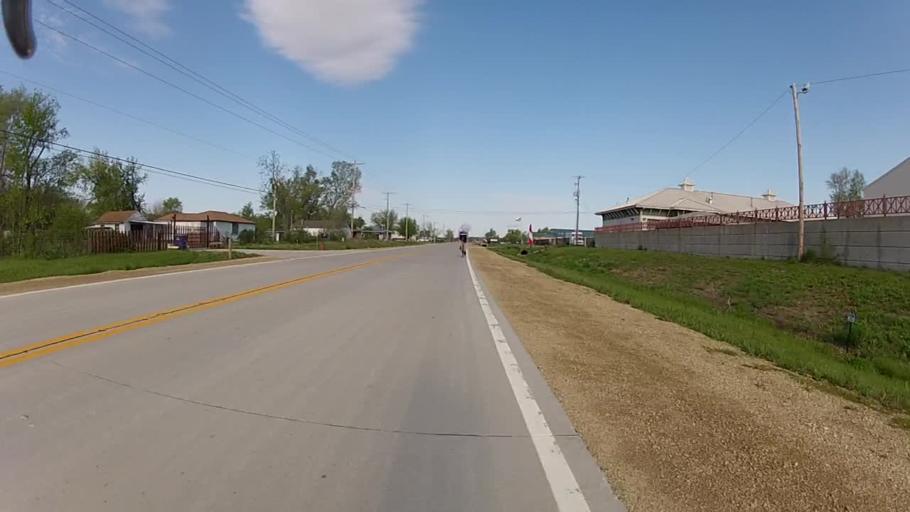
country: US
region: Kansas
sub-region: Riley County
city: Ogden
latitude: 39.1530
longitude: -96.6539
